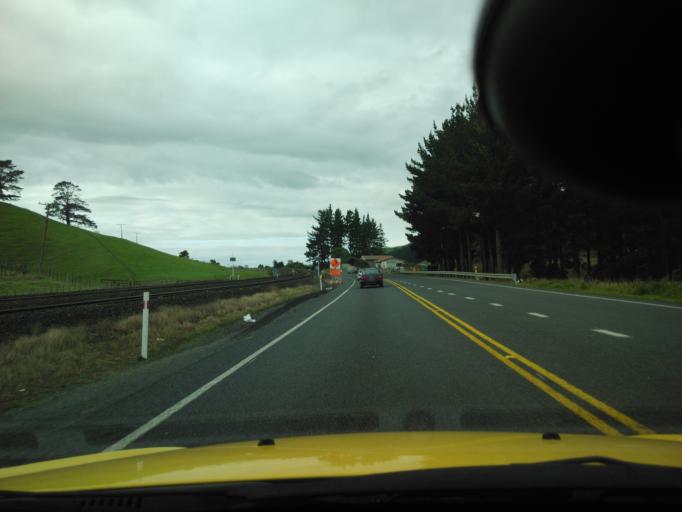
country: NZ
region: Waikato
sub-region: Waikato District
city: Ngaruawahia
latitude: -37.5979
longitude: 175.1633
